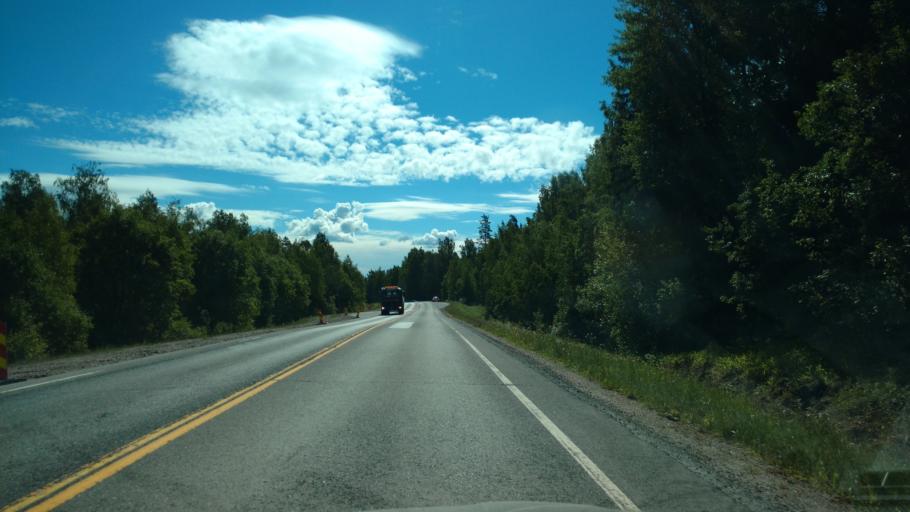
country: FI
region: Varsinais-Suomi
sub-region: Salo
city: Muurla
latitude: 60.3814
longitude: 23.2448
